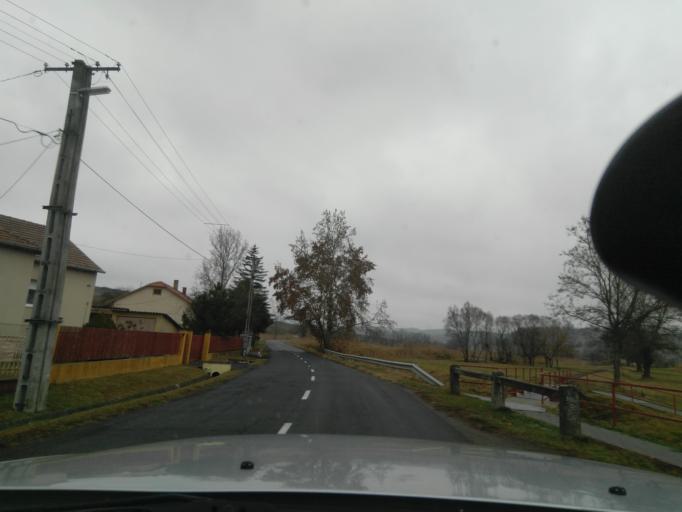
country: HU
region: Nograd
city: Kazar
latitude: 48.0320
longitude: 19.8727
